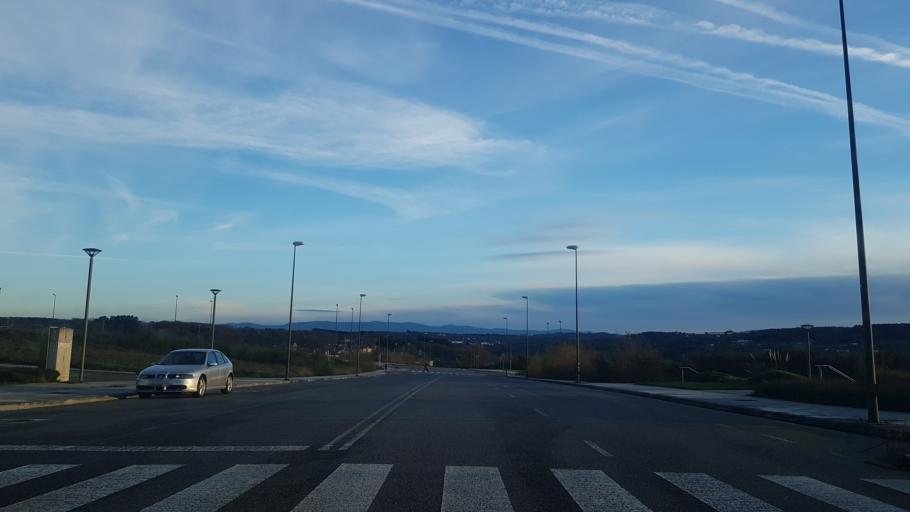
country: ES
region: Galicia
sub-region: Provincia de Lugo
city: Lugo
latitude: 42.9977
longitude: -7.5423
